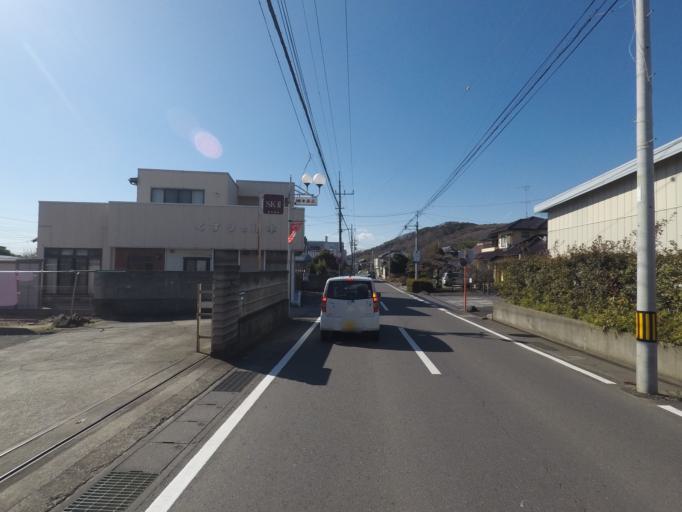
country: JP
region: Ibaraki
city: Tsukuba
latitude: 36.1764
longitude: 140.0966
